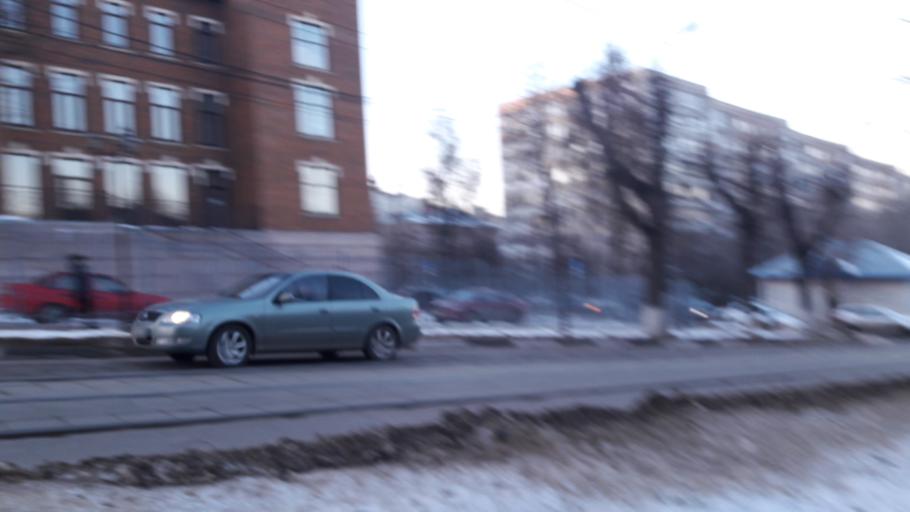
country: RU
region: Tula
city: Tula
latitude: 54.1880
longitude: 37.6082
